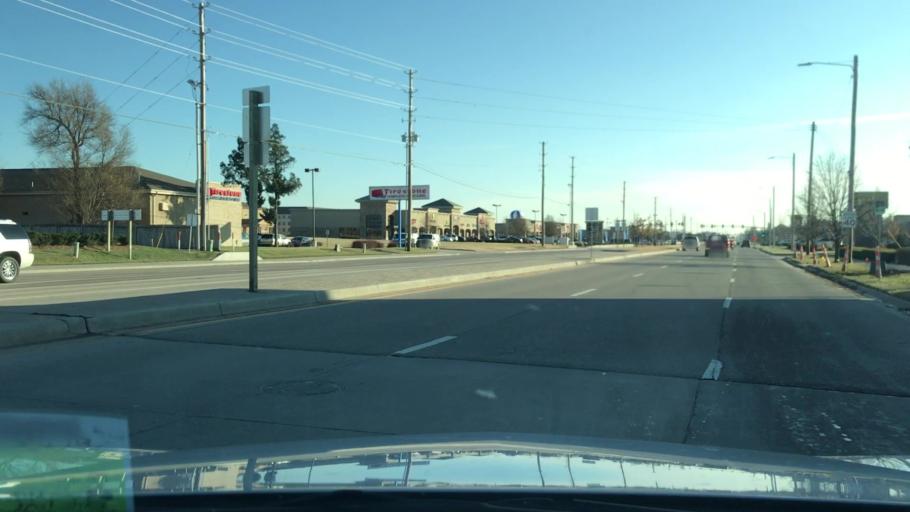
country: US
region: Kansas
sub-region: Sedgwick County
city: Bellaire
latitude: 37.7280
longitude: -97.2080
